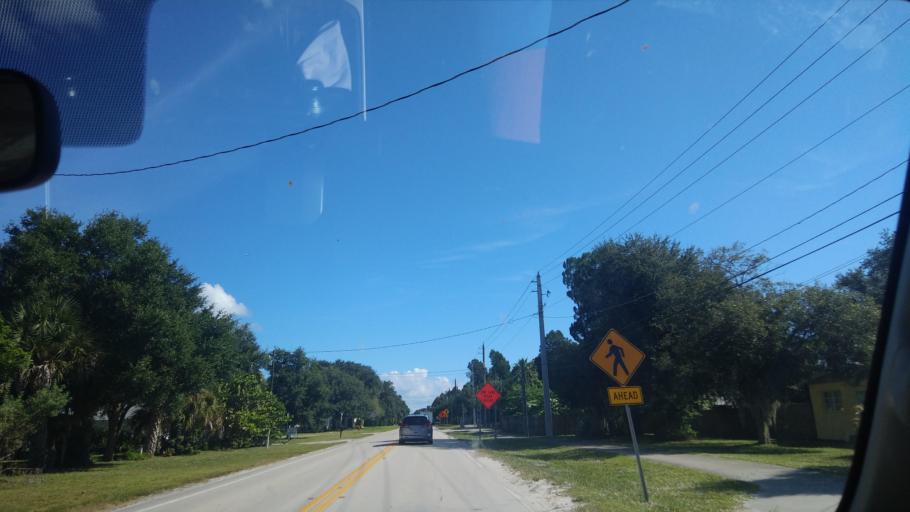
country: US
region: Florida
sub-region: Indian River County
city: Roseland
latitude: 27.8329
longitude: -80.4957
